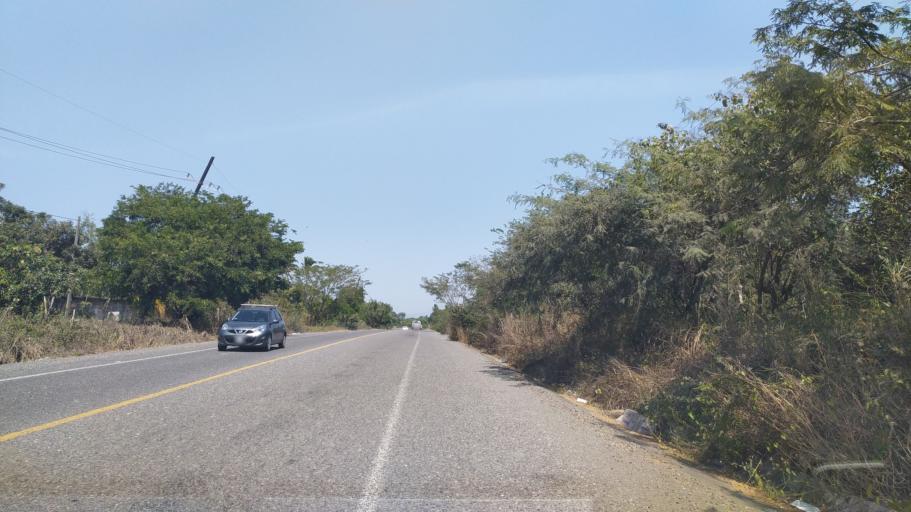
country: MX
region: Michoacan
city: Coahuayana Viejo
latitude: 18.6564
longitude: -103.6695
